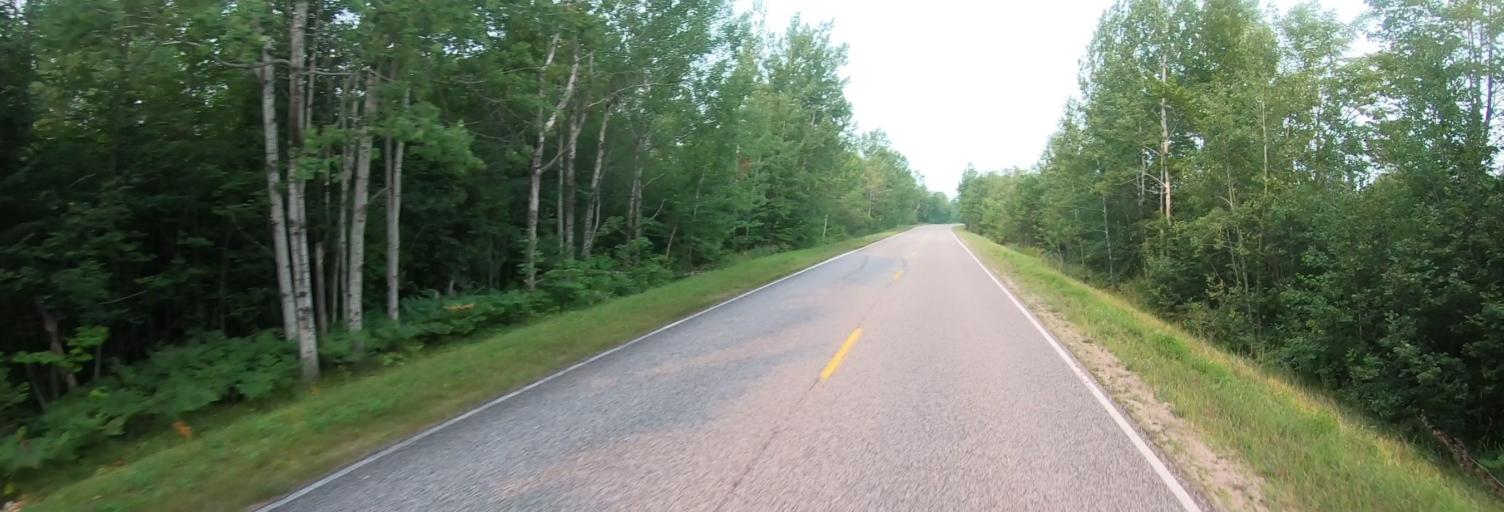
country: US
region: Michigan
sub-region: Chippewa County
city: Sault Ste. Marie
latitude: 46.4649
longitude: -84.8872
